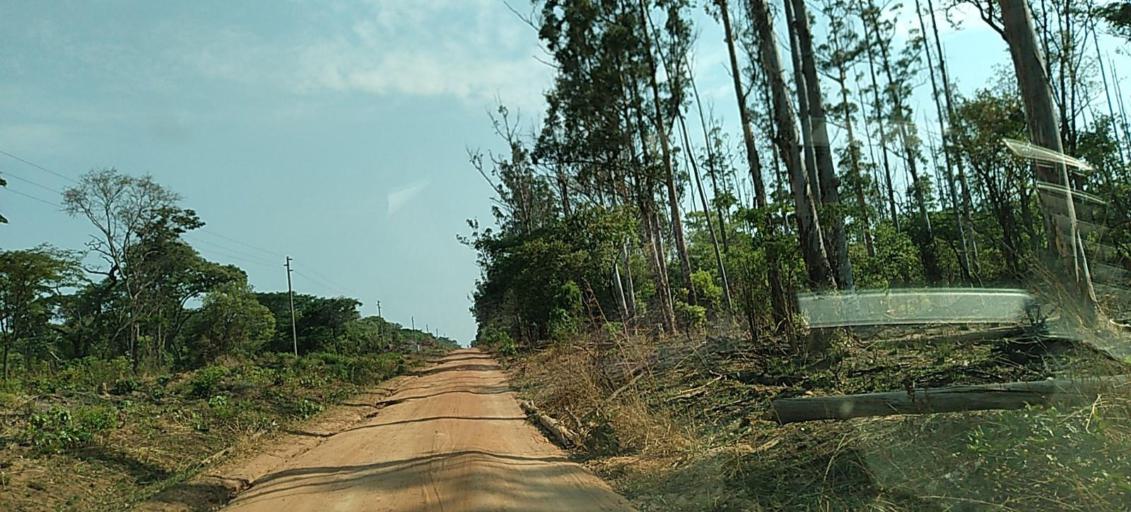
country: ZM
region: Copperbelt
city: Kalulushi
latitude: -13.0011
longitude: 27.8136
